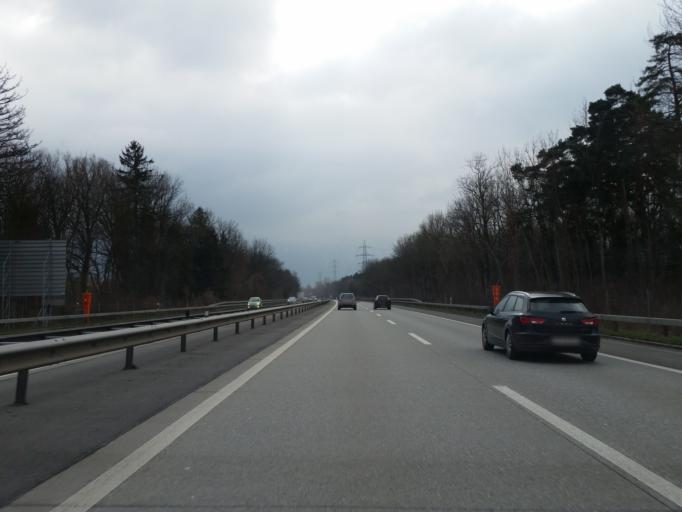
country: CH
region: Saint Gallen
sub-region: Wahlkreis Werdenberg
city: Buchs
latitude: 47.1623
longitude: 9.4899
